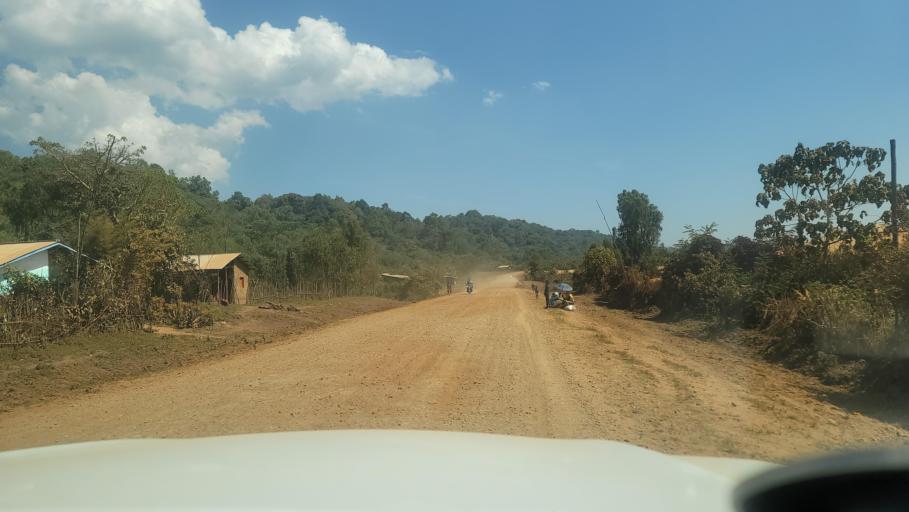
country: ET
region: Oromiya
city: Agaro
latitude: 7.7751
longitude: 36.3266
